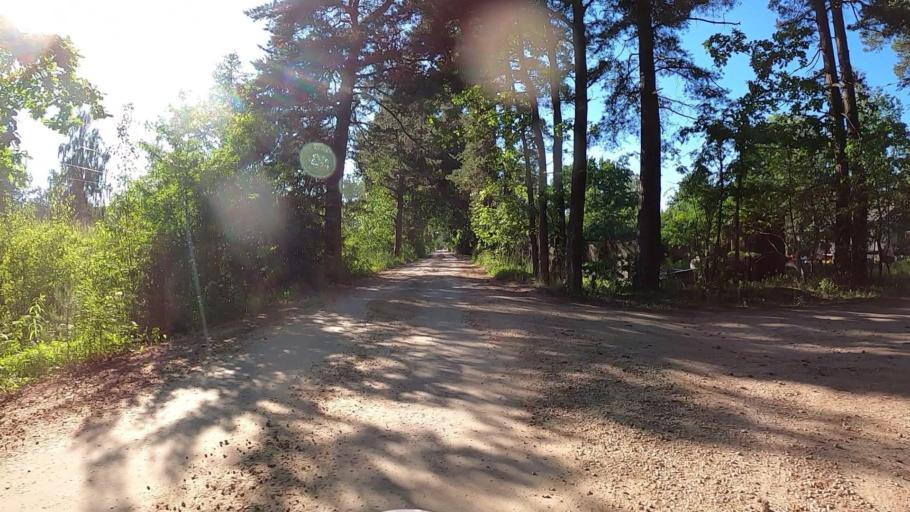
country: LV
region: Kekava
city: Kekava
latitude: 56.8747
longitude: 24.2709
